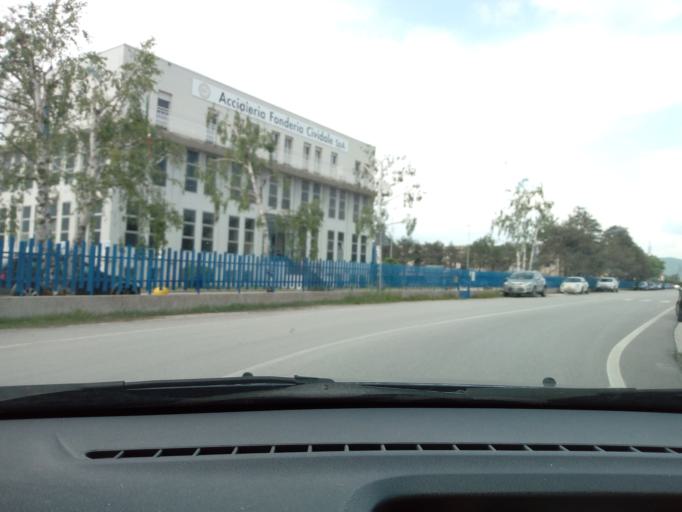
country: IT
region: Friuli Venezia Giulia
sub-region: Provincia di Udine
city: Moimacco
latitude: 46.0878
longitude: 13.3942
